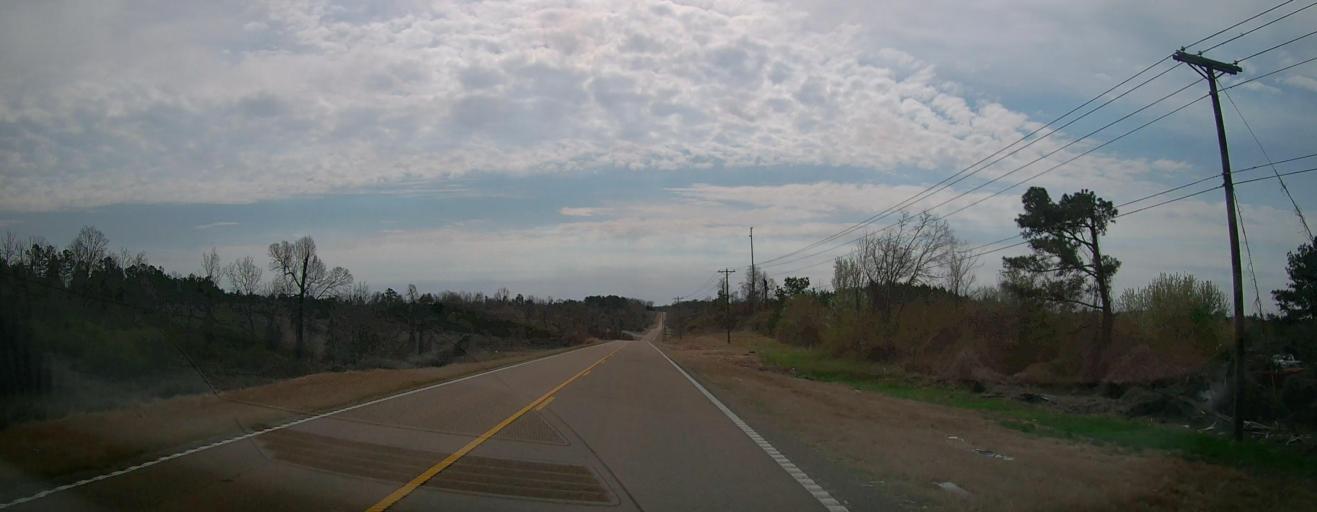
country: US
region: Mississippi
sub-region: Marshall County
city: Holly Springs
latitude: 34.7498
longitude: -89.4289
